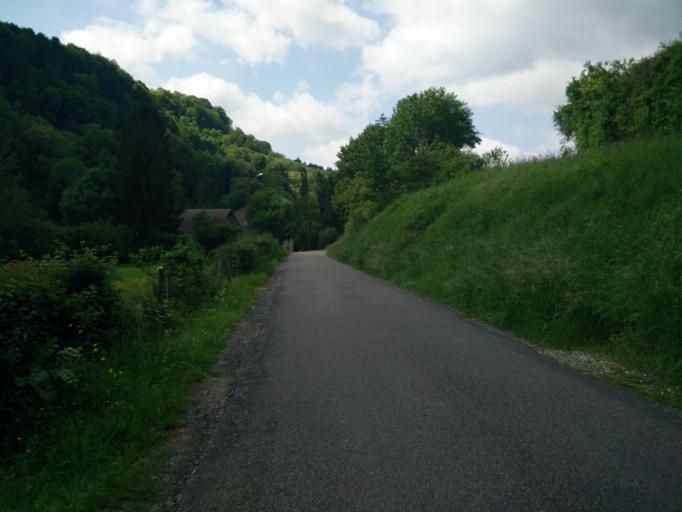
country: FR
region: Franche-Comte
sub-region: Departement du Jura
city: Lons-le-Saunier
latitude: 46.6373
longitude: 5.5442
